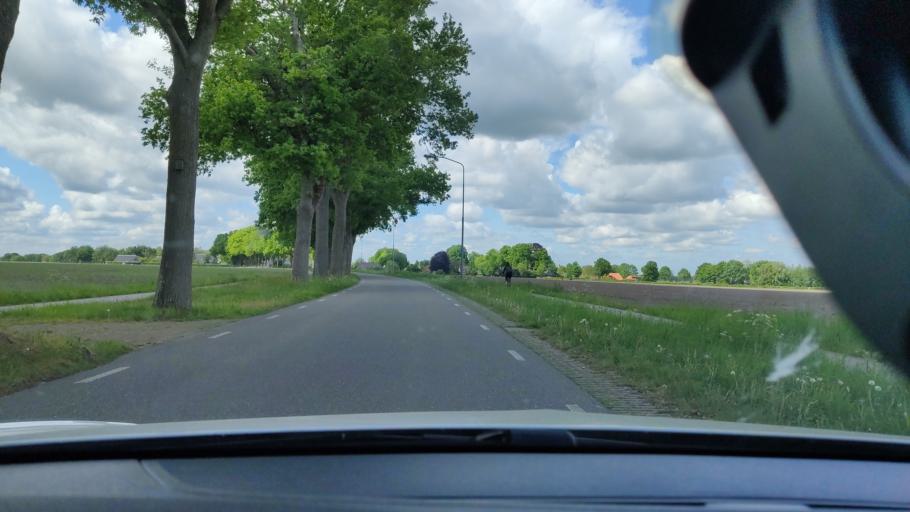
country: NL
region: Drenthe
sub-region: Gemeente Tynaarlo
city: Zuidlaren
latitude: 53.1144
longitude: 6.6731
